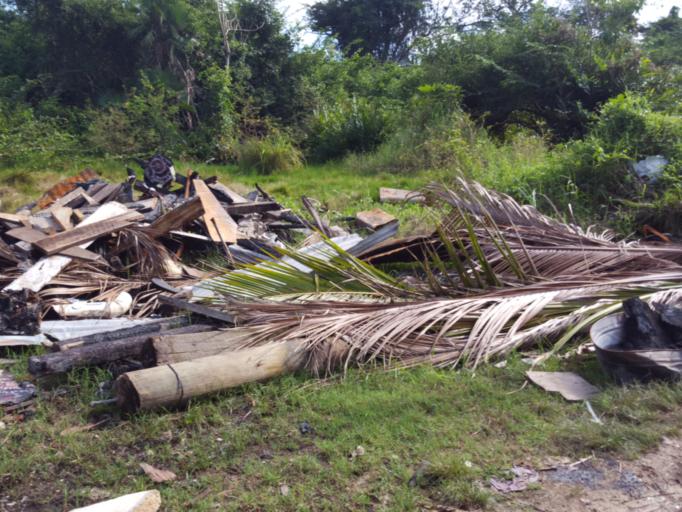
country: BZ
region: Belize
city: Belize City
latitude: 17.5695
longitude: -88.3978
